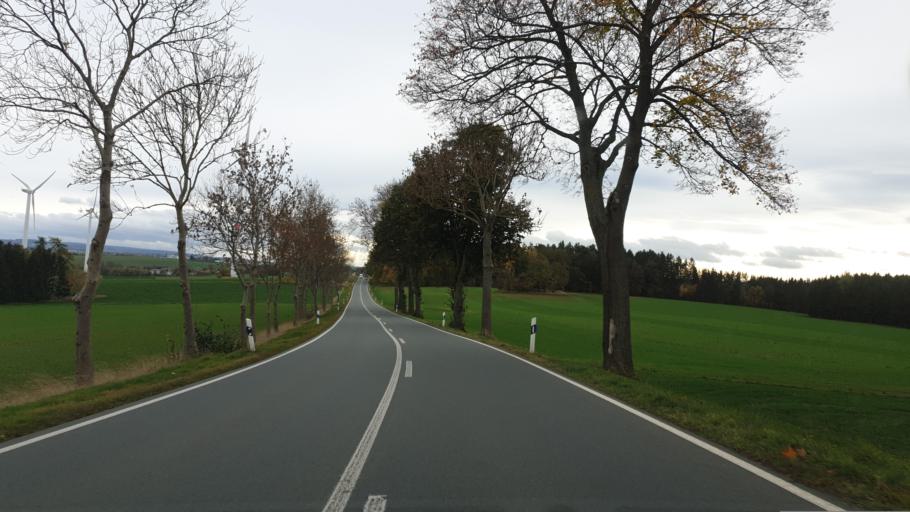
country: DE
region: Saxony
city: Limbach
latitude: 50.5772
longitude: 12.2741
